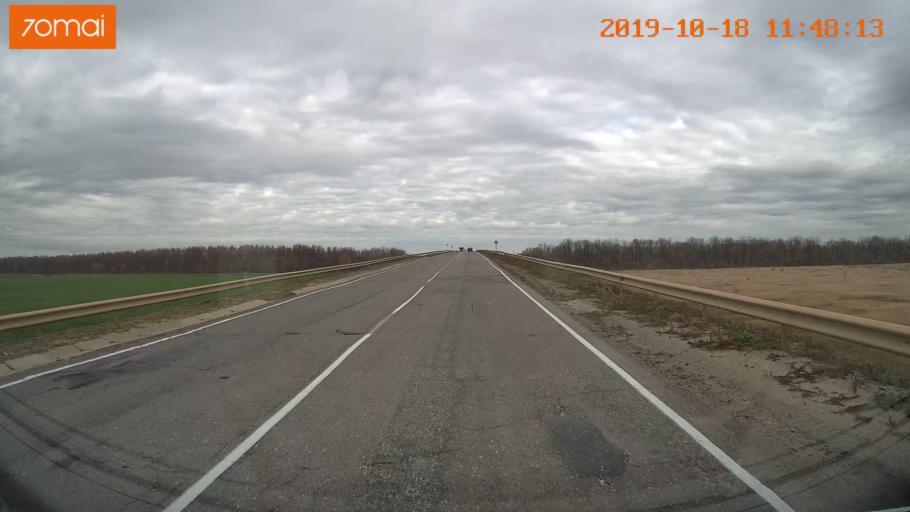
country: RU
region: Rjazan
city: Mikhaylov
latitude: 54.2373
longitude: 38.9817
